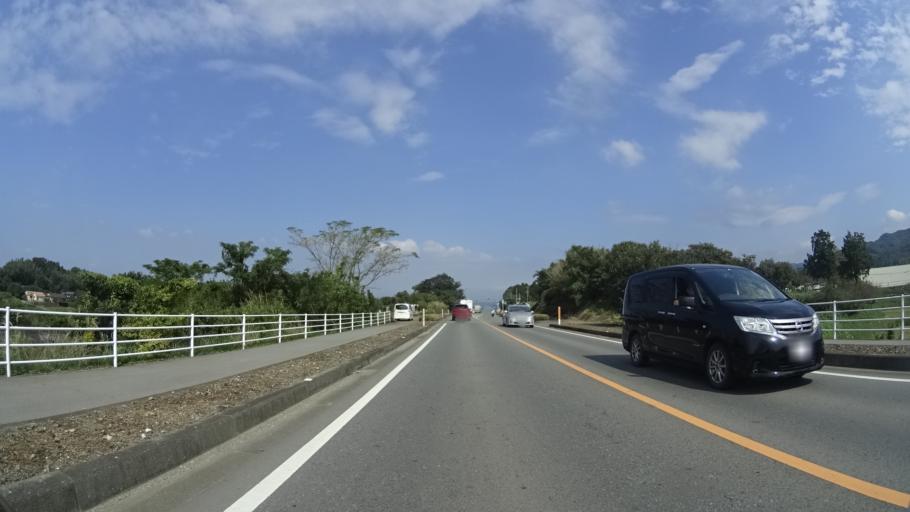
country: JP
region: Kumamoto
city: Kumamoto
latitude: 32.7520
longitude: 130.8022
